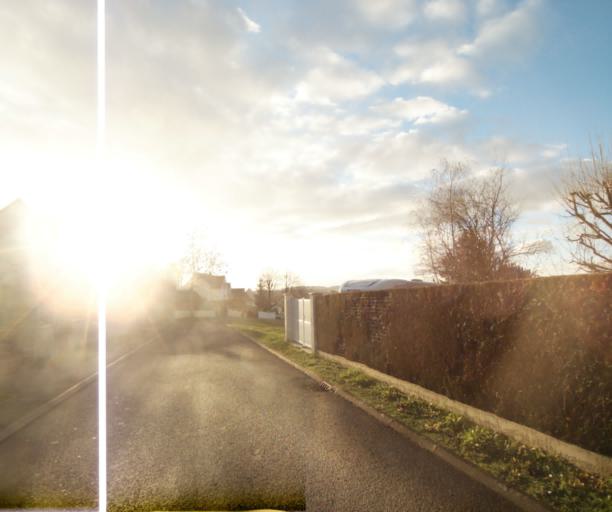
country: FR
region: Ile-de-France
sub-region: Departement des Yvelines
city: Meulan-en-Yvelines
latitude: 49.0143
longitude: 1.9182
